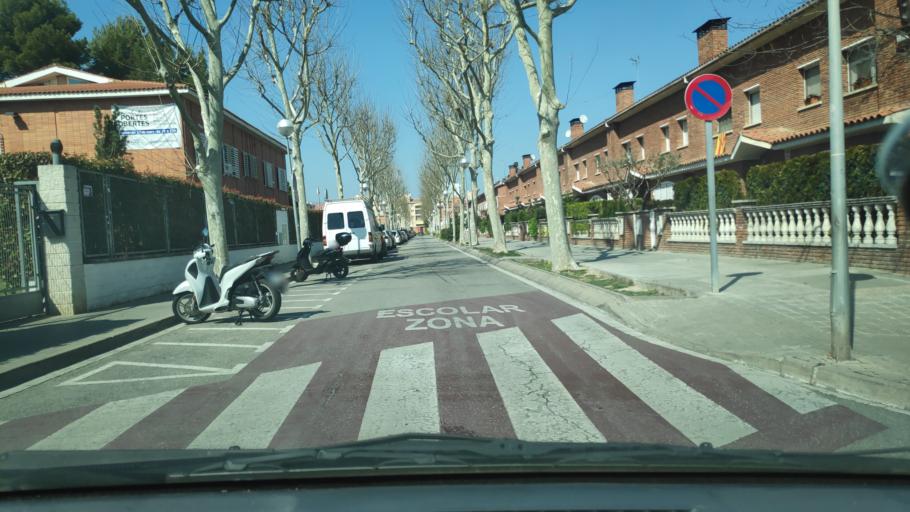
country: ES
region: Catalonia
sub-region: Provincia de Barcelona
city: Mollet del Valles
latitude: 41.5429
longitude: 2.2046
